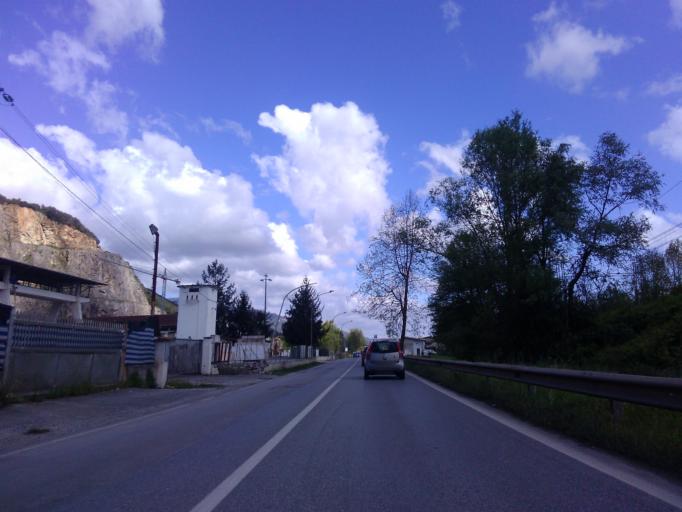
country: IT
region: Tuscany
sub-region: Provincia di Massa-Carrara
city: Capanne-Prato-Cinquale
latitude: 43.9963
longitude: 10.1742
